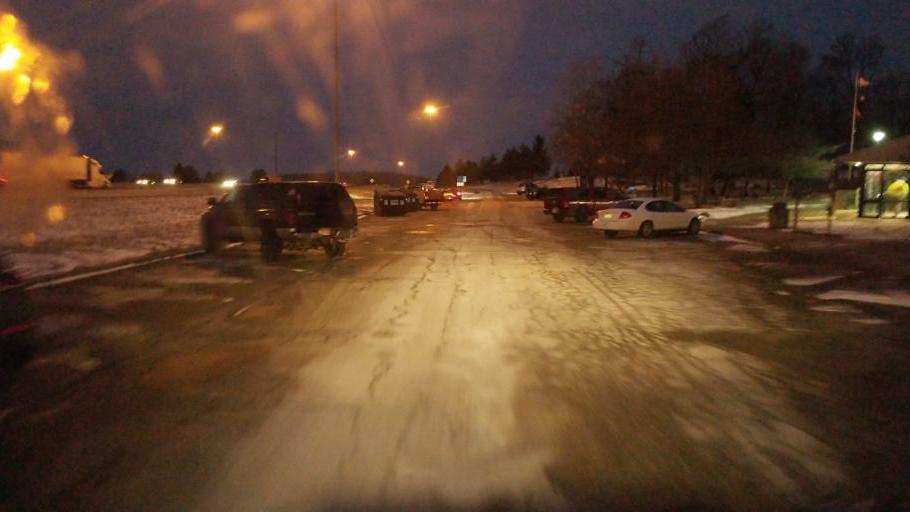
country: US
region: Ohio
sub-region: Preble County
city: New Paris
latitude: 39.8293
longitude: -84.7586
